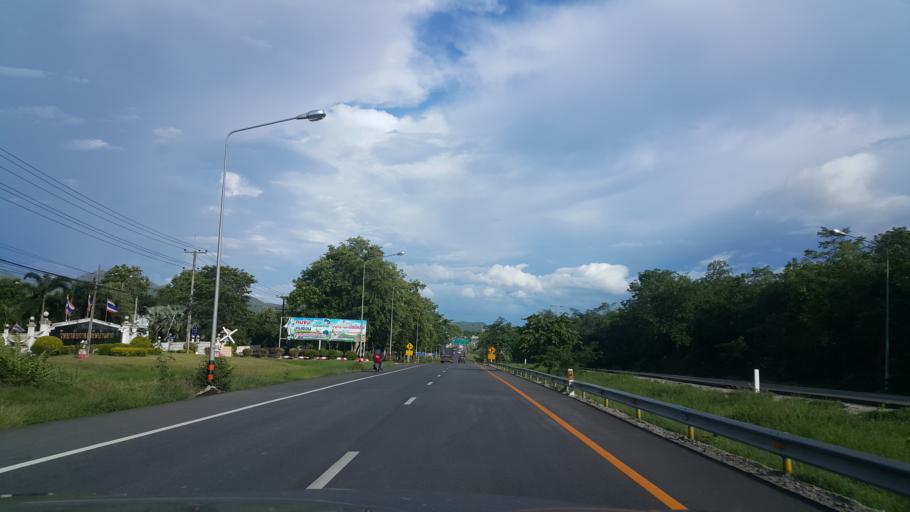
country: TH
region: Tak
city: Ban Tak
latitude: 17.0401
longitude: 99.0842
